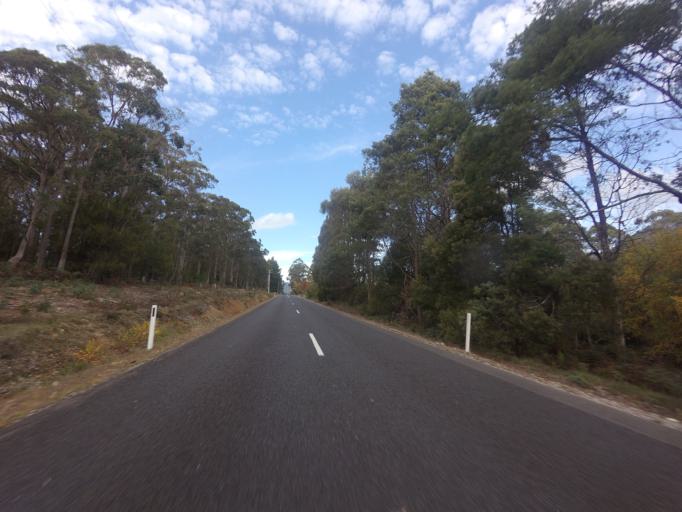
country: AU
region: Tasmania
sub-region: Meander Valley
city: Deloraine
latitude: -41.6196
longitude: 146.6968
